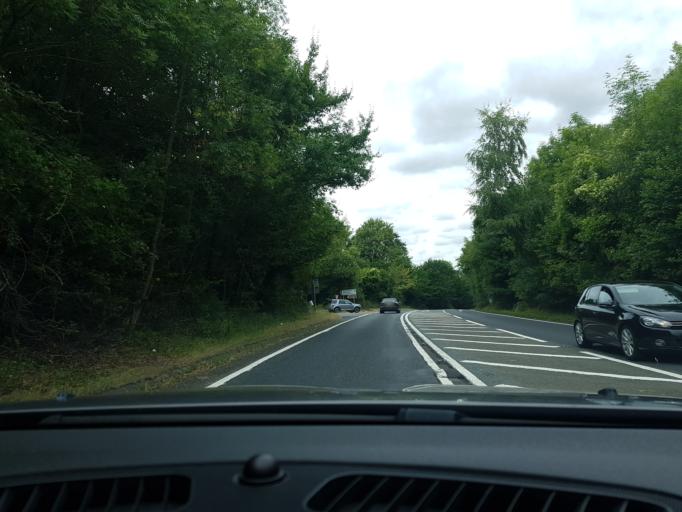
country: GB
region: England
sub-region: Hampshire
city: Kingsclere
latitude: 51.3170
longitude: -1.2086
